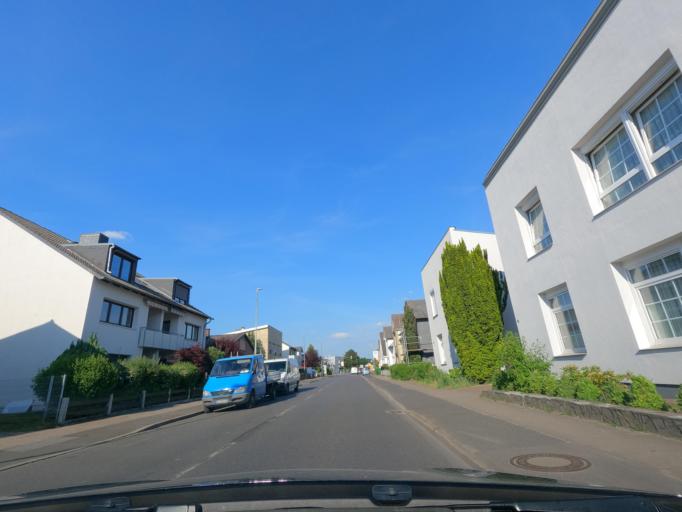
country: DE
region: Schleswig-Holstein
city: Uetersen
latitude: 53.6893
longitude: 9.6833
